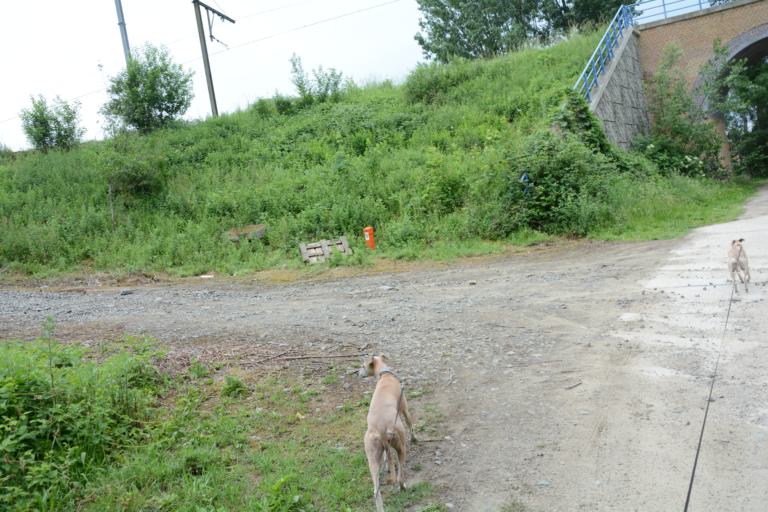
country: BE
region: Flanders
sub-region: Provincie Oost-Vlaanderen
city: Melle
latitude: 50.9902
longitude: 3.8099
